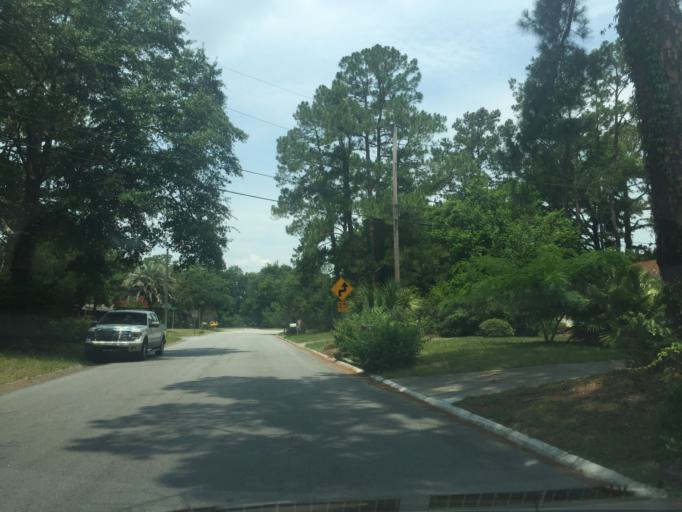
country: US
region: Georgia
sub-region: Chatham County
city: Montgomery
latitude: 31.9869
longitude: -81.1270
